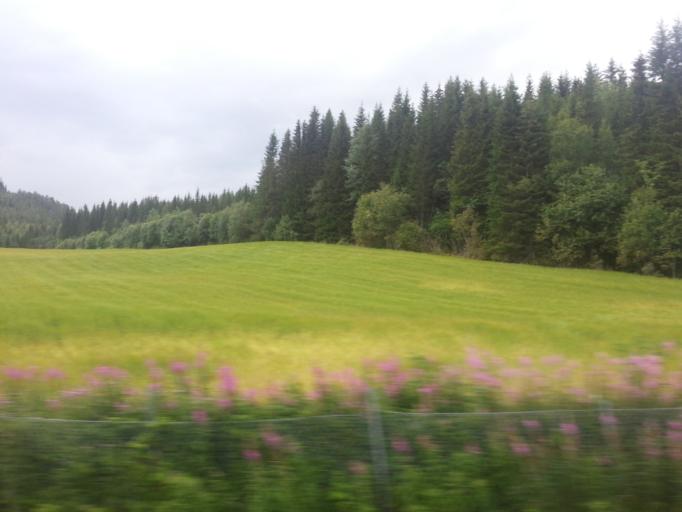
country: NO
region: Sor-Trondelag
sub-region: Malvik
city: Hommelvik
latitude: 63.4127
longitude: 10.7702
